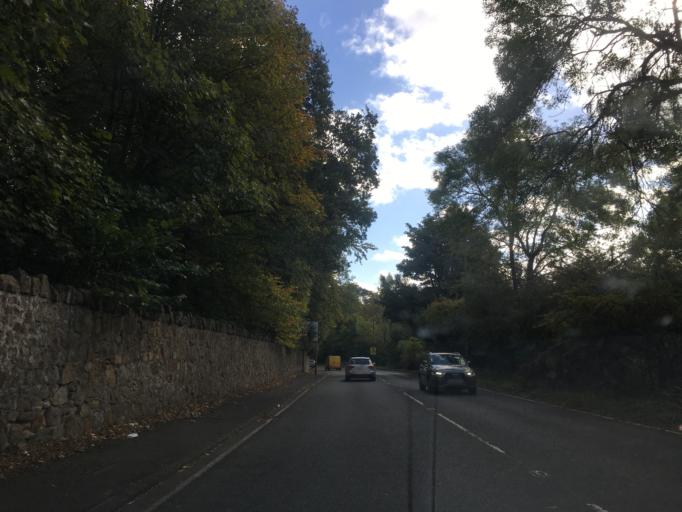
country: GB
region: Scotland
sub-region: Midlothian
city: Bonnyrigg
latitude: 55.8844
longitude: -3.1275
